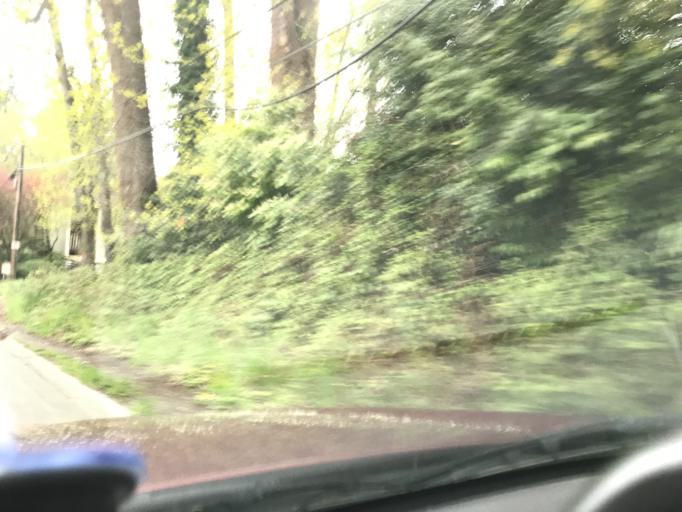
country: US
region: Washington
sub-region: King County
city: Lake Forest Park
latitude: 47.6976
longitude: -122.3034
